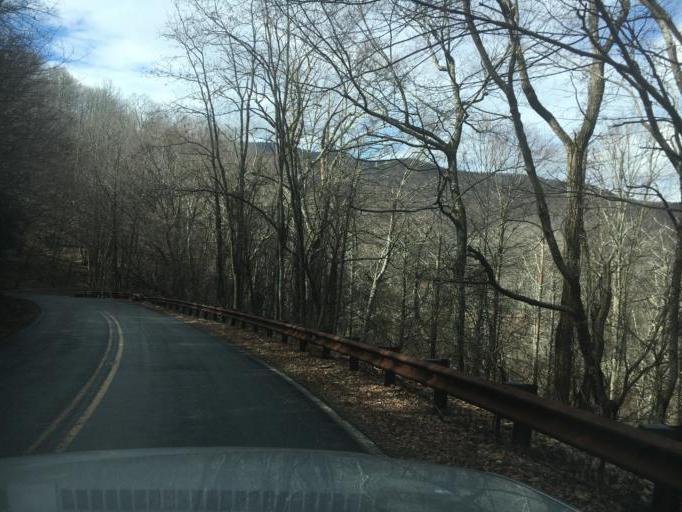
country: US
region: North Carolina
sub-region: Transylvania County
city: Brevard
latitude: 35.3709
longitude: -82.8053
